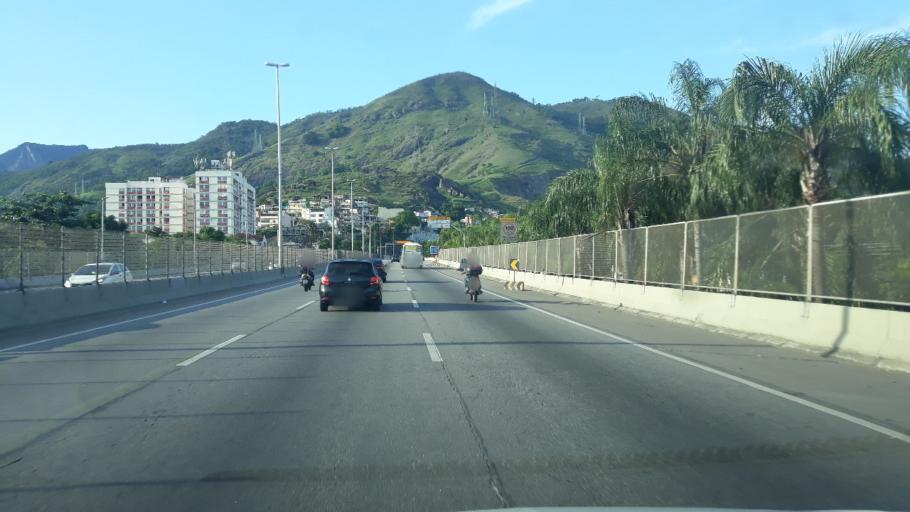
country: BR
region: Rio de Janeiro
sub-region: Rio De Janeiro
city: Rio de Janeiro
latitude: -22.9025
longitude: -43.3040
